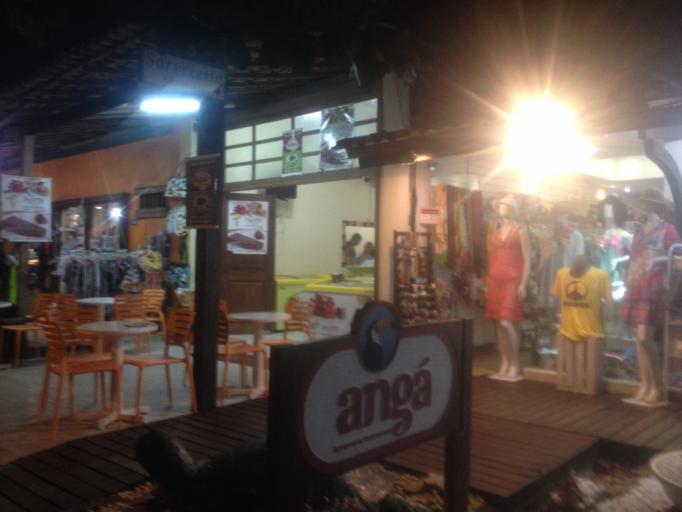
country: BR
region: Bahia
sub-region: Mata De Sao Joao
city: Mata de Sao Joao
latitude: -12.5775
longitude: -38.0043
